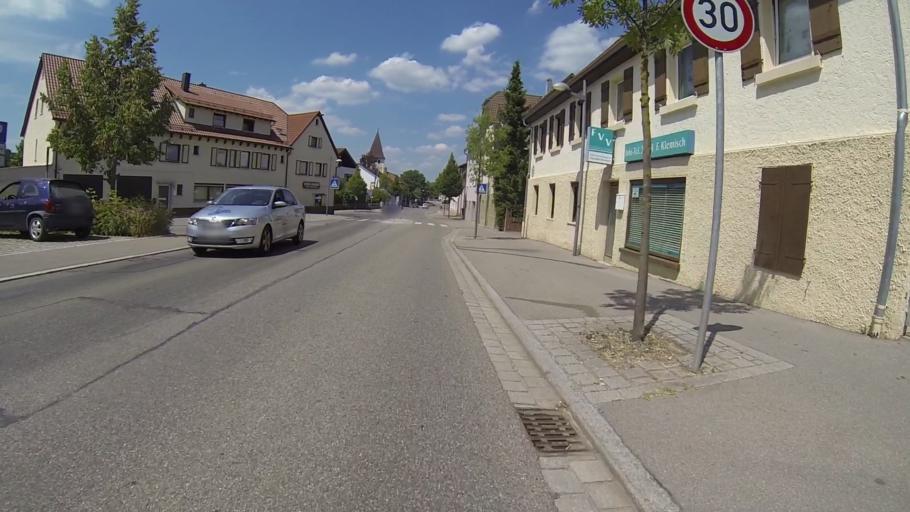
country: DE
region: Baden-Wuerttemberg
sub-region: Regierungsbezirk Stuttgart
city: Herbrechtingen
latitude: 48.6191
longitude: 10.1808
